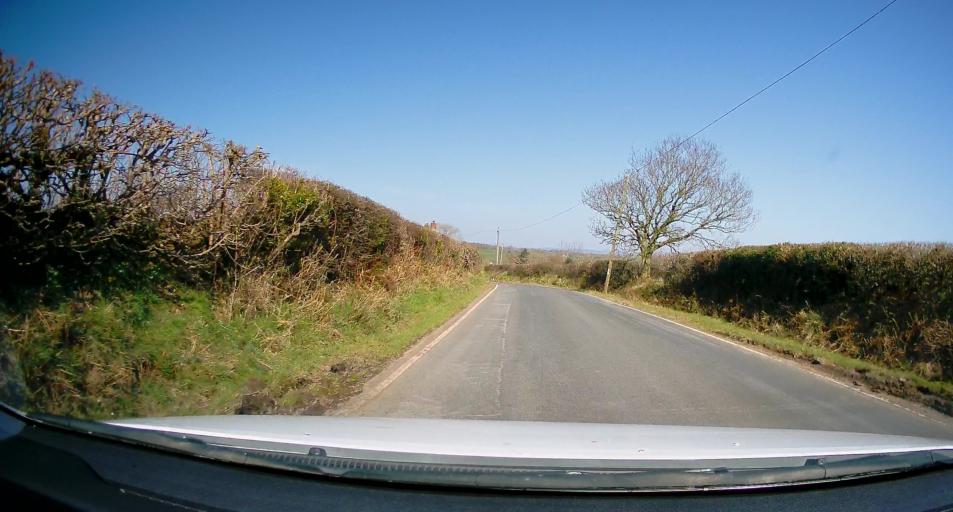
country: GB
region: Wales
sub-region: County of Ceredigion
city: Lledrod
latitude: 52.3076
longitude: -4.0647
